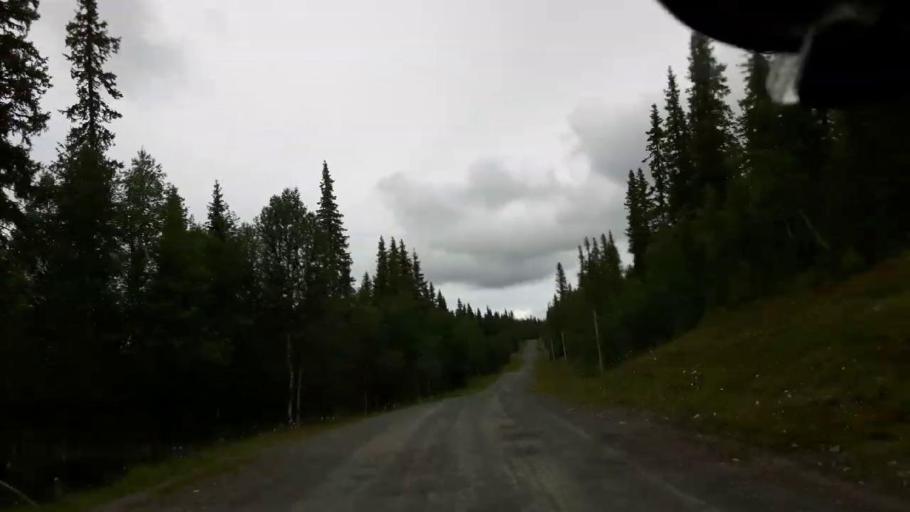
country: SE
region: Jaemtland
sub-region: Krokoms Kommun
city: Valla
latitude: 63.7470
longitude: 13.8355
